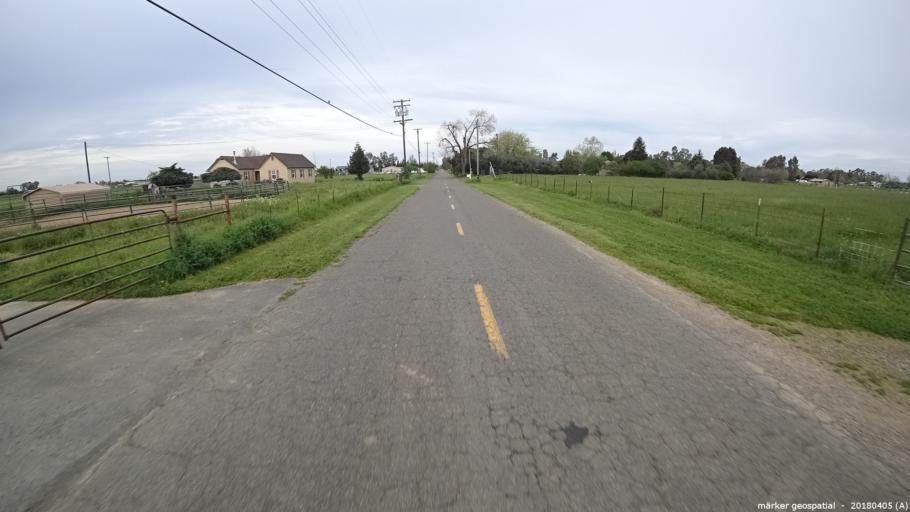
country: US
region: California
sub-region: Sacramento County
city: Herald
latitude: 38.2776
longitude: -121.2279
